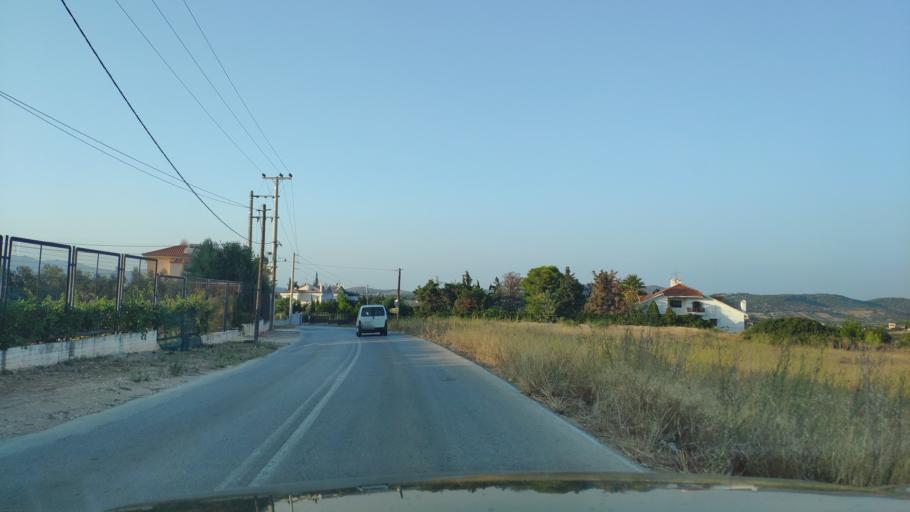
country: GR
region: Attica
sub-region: Nomarchia Anatolikis Attikis
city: Markopoulo
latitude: 37.9065
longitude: 23.9616
